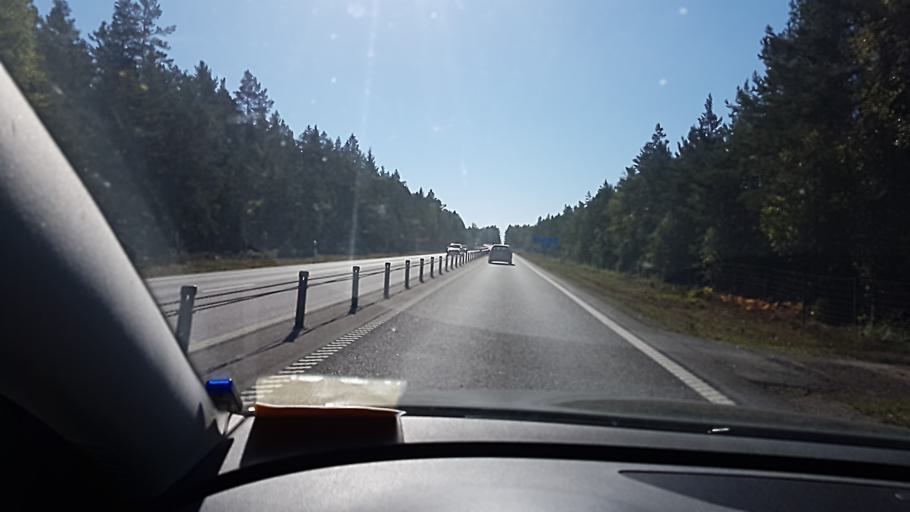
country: SE
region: Kronoberg
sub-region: Lessebo Kommun
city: Hovmantorp
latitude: 56.8012
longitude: 15.1140
